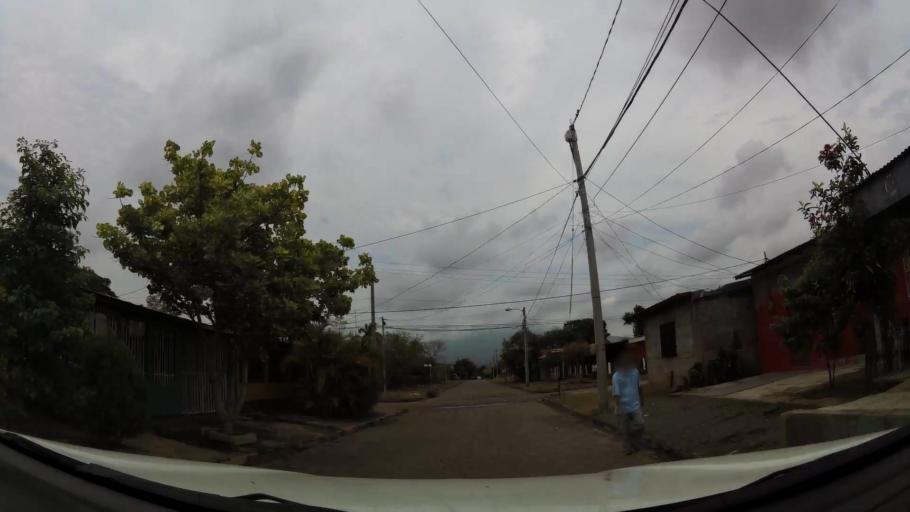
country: NI
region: Granada
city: Granada
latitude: 11.9342
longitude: -85.9659
